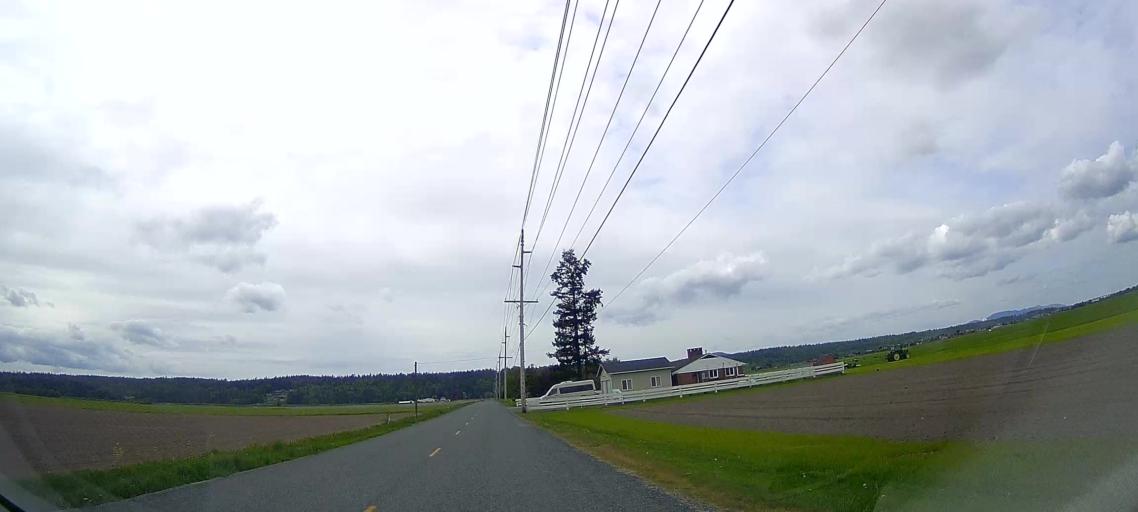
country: US
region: Washington
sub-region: Skagit County
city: Mount Vernon
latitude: 48.4210
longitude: -122.4775
